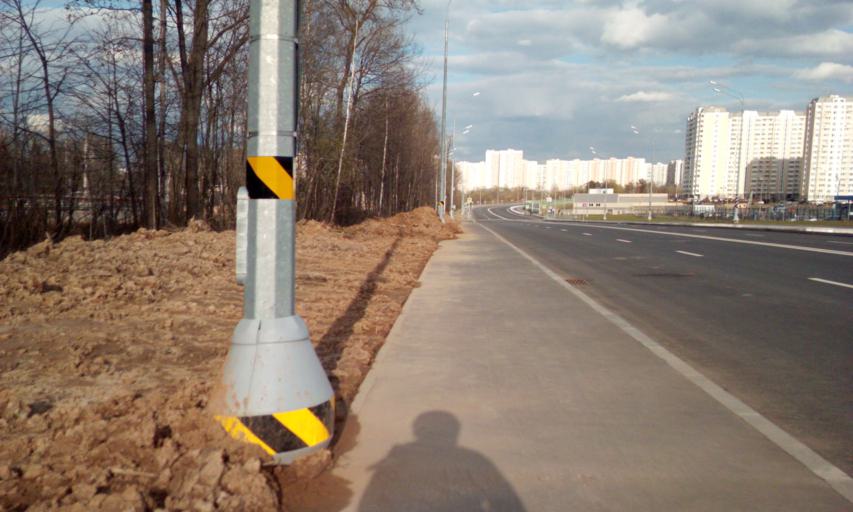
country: RU
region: Moscow
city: Novo-Peredelkino
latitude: 55.6458
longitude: 37.3197
